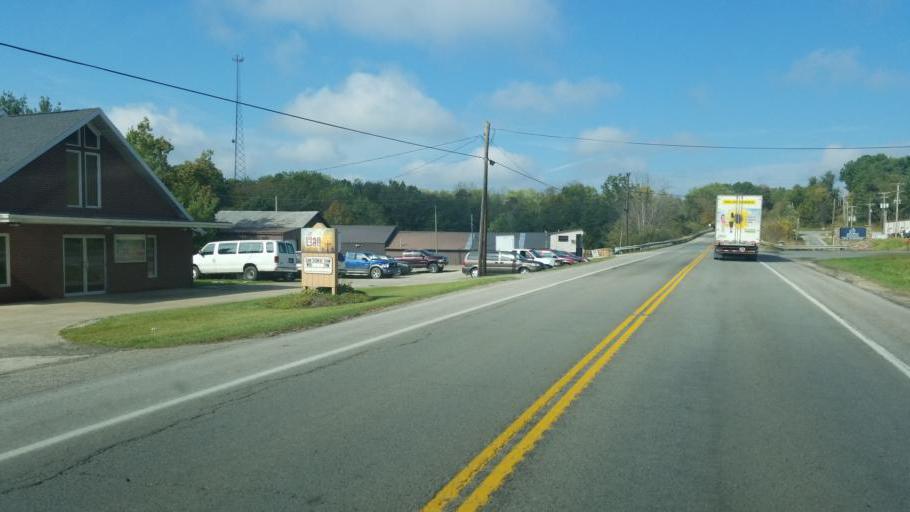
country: US
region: Ohio
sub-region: Stark County
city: Brewster
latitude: 40.6752
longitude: -81.6629
